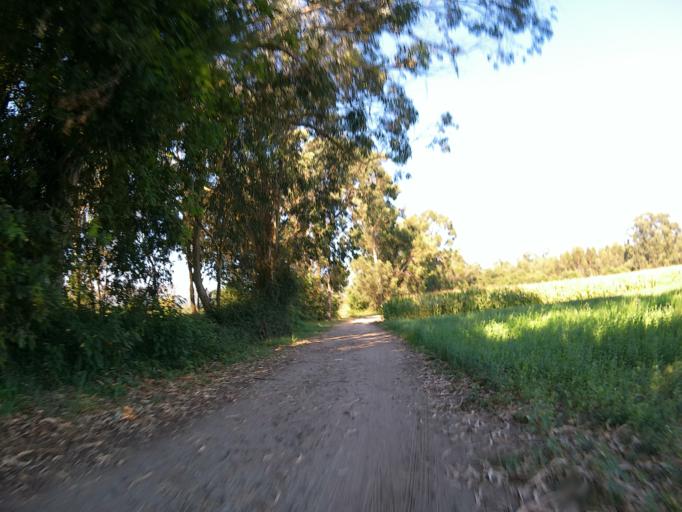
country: PT
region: Viana do Castelo
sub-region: Ponte de Lima
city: Ponte de Lima
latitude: 41.7578
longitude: -8.6211
